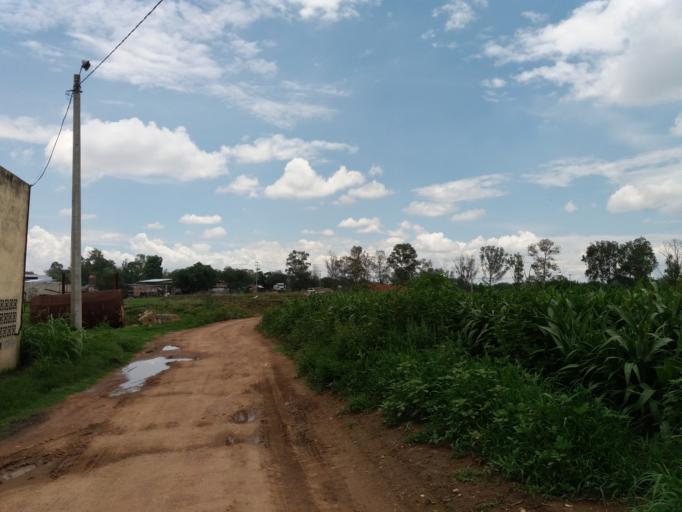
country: MX
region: Aguascalientes
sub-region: Aguascalientes
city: La Loma de los Negritos
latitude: 21.8317
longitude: -102.3319
